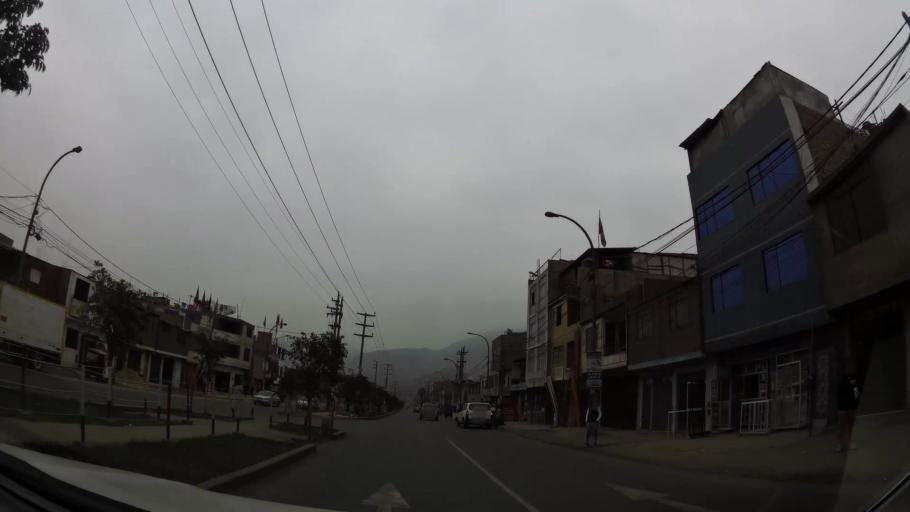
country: PE
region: Lima
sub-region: Lima
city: Independencia
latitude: -11.9559
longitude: -76.9939
